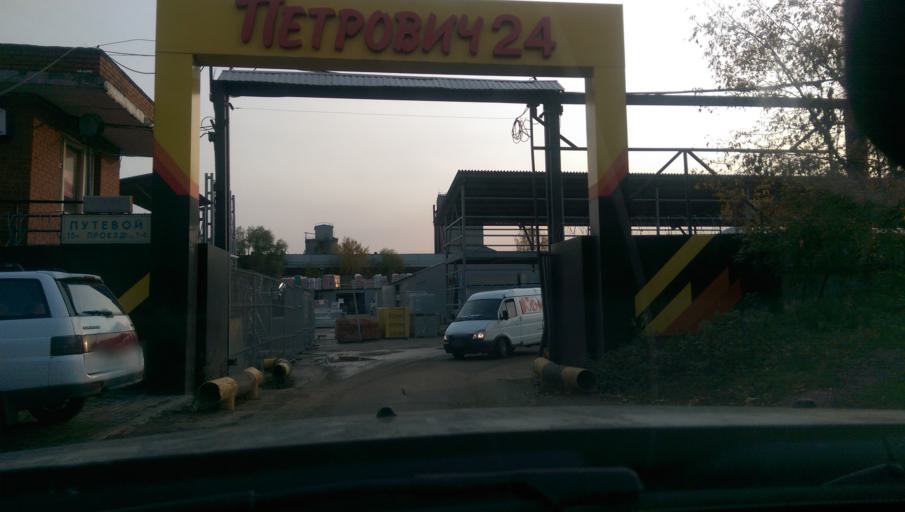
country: RU
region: Moscow
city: Altuf'yevskiy
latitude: 55.8874
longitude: 37.5734
